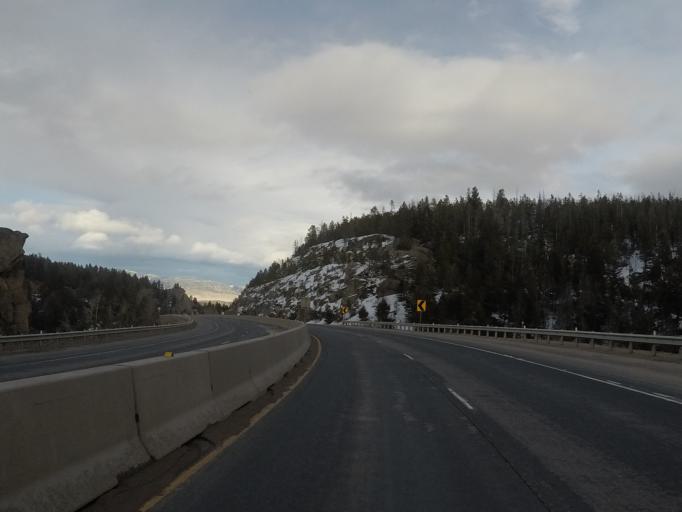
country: US
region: Montana
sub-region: Silver Bow County
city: Butte
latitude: 45.9108
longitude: -112.3514
